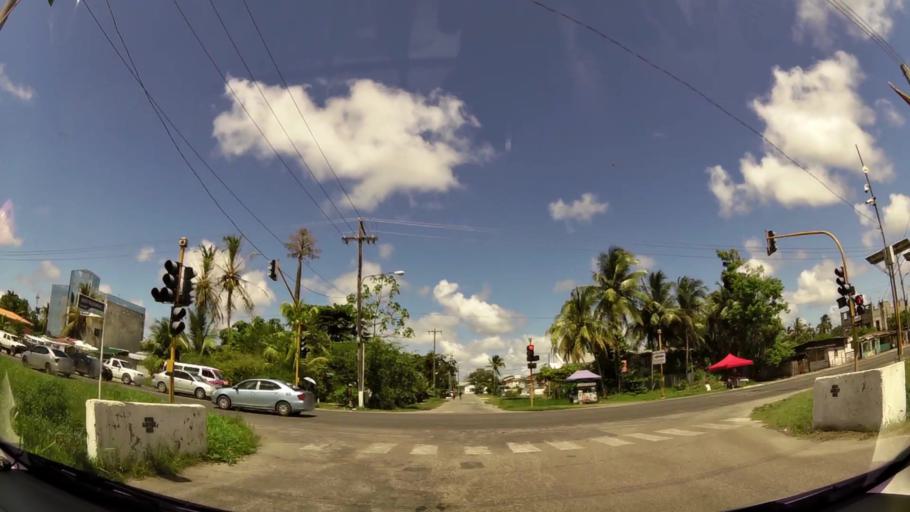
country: GY
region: Demerara-Mahaica
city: Georgetown
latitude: 6.7996
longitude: -58.1402
